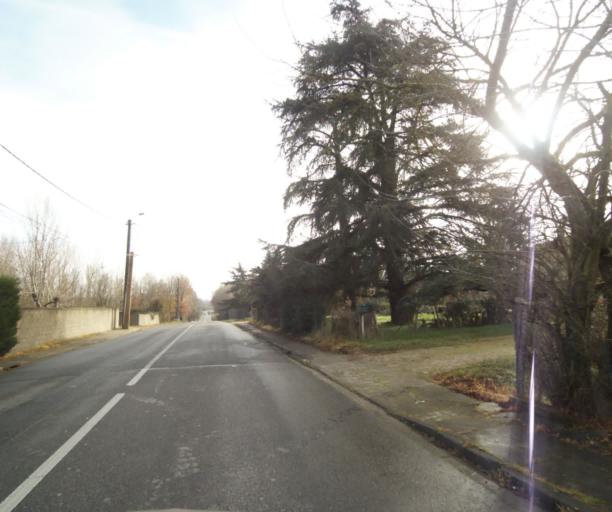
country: FR
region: Midi-Pyrenees
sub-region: Departement de la Haute-Garonne
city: Villemur-sur-Tarn
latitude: 43.8589
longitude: 1.4835
